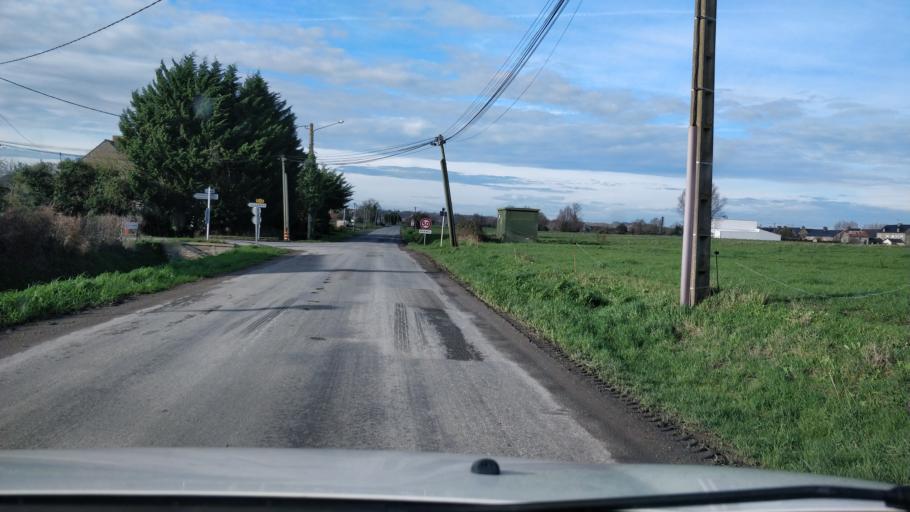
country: FR
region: Brittany
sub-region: Departement d'Ille-et-Vilaine
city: La Fresnais
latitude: 48.5798
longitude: -1.8585
